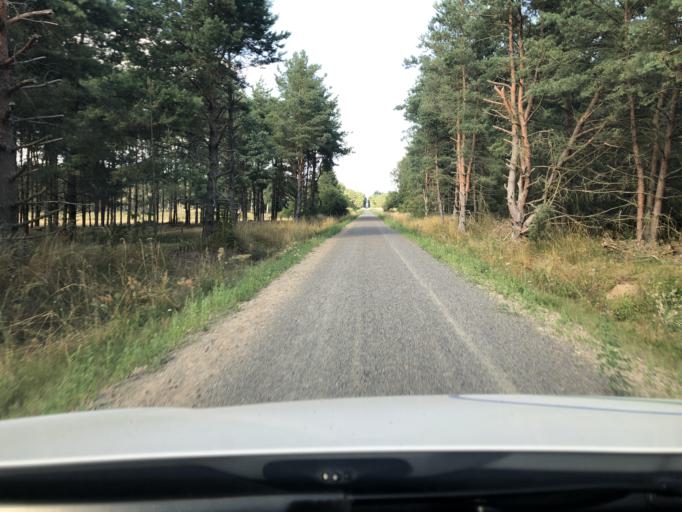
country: SE
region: Skane
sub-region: Kristianstads Kommun
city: Norra Asum
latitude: 55.9184
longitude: 14.1205
